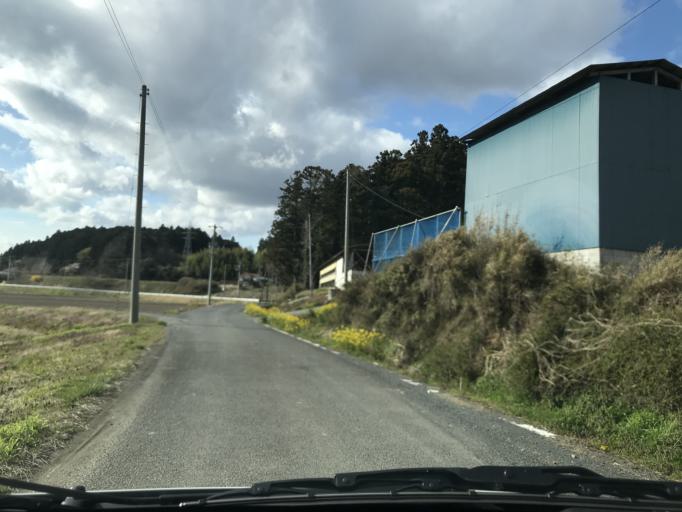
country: JP
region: Miyagi
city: Wakuya
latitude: 38.6104
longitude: 141.2340
